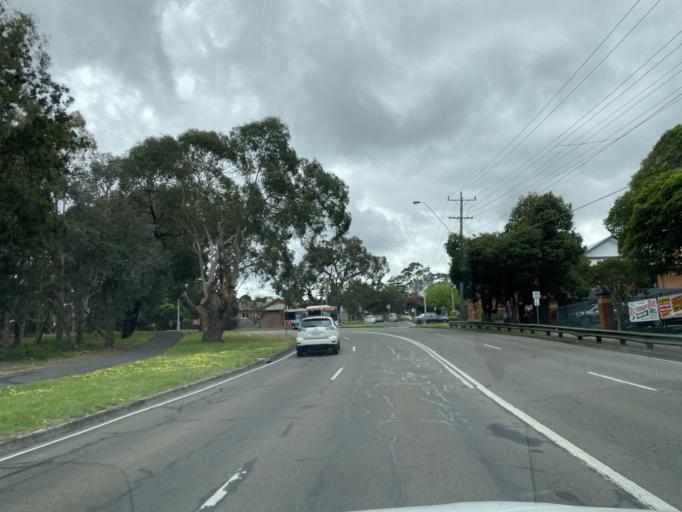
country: AU
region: Victoria
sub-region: Whitehorse
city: Box Hill South
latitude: -37.8405
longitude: 145.1217
